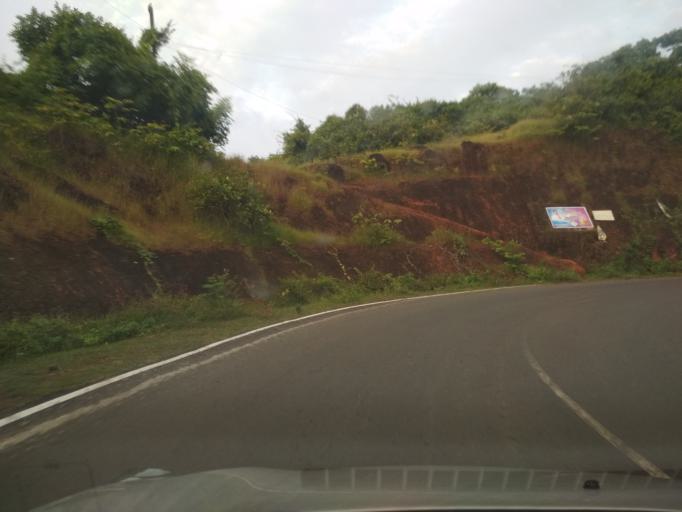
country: IN
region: Goa
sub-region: North Goa
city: Morjim
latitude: 15.6492
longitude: 73.7600
